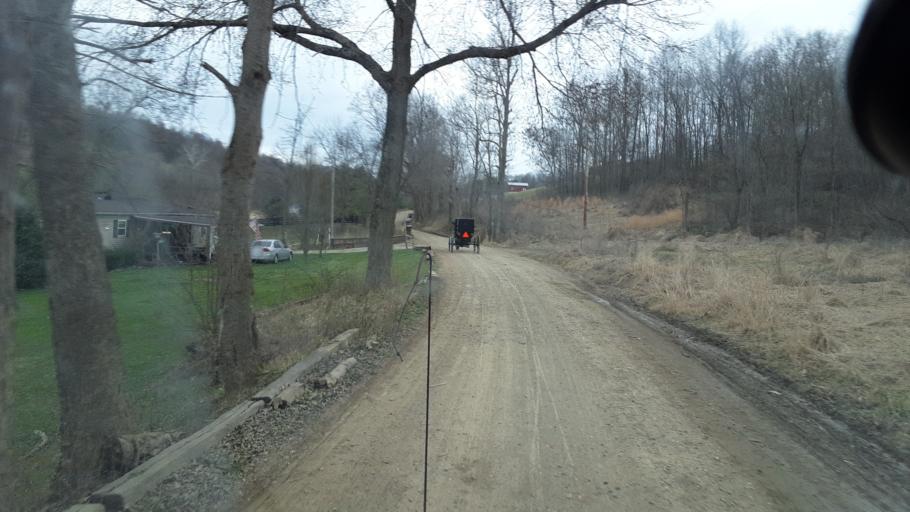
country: US
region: Ohio
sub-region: Coshocton County
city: West Lafayette
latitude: 40.3541
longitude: -81.7686
